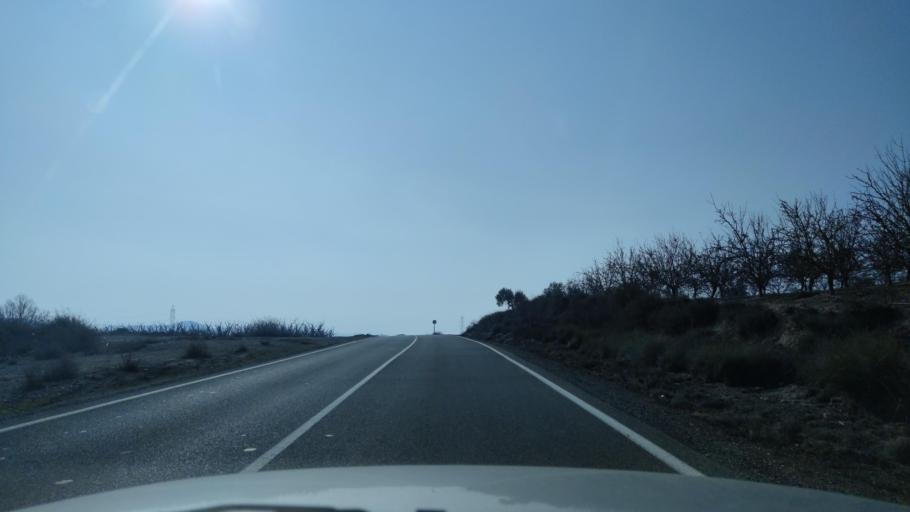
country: ES
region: Catalonia
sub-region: Provincia de Lleida
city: Seros
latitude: 41.4699
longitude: 0.3795
